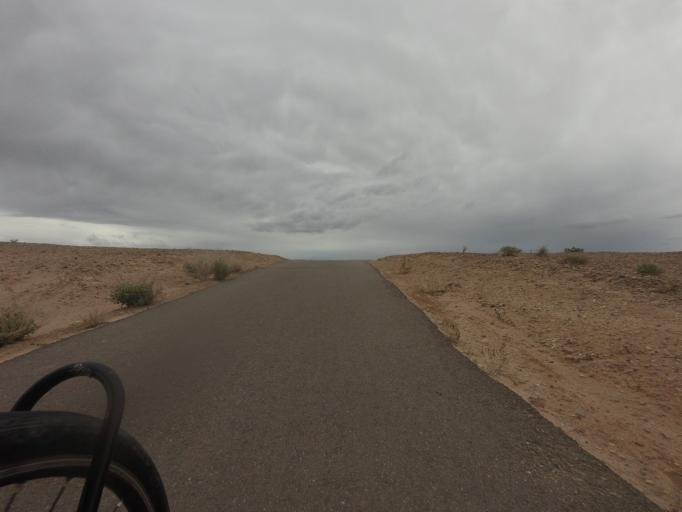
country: US
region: Nevada
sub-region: Clark County
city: Henderson
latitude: 36.1025
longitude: -114.9978
